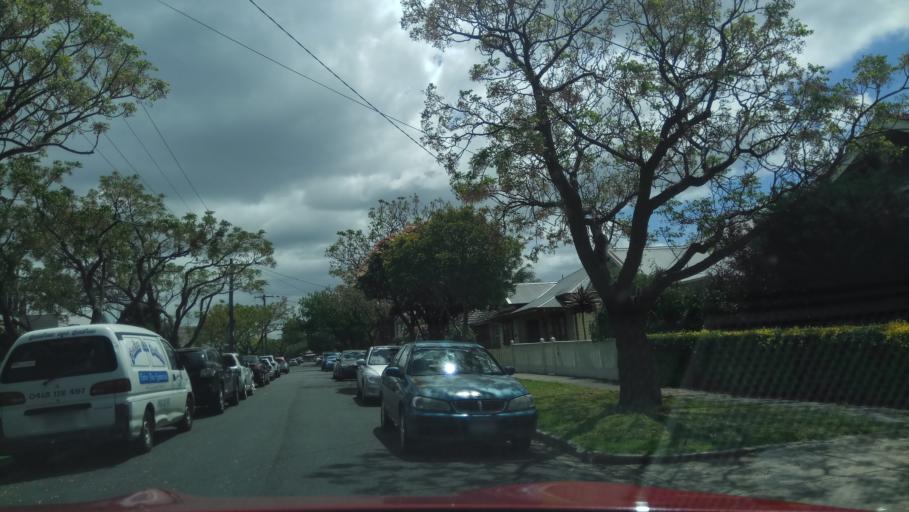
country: AU
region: Victoria
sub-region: Hobsons Bay
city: Newport
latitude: -37.8489
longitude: 144.8891
